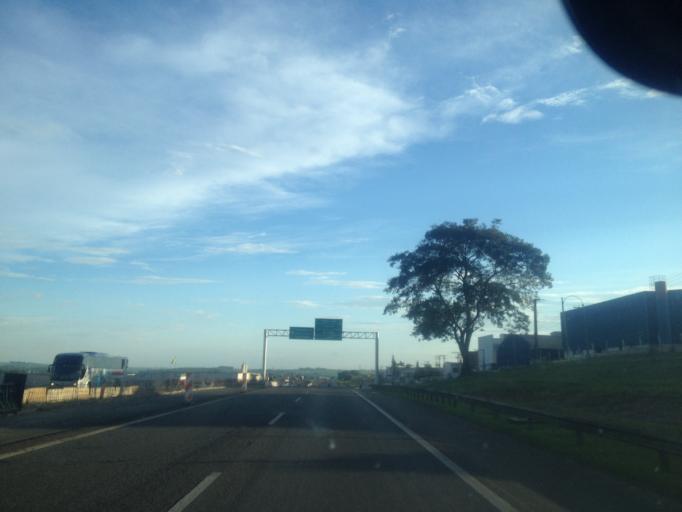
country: BR
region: Sao Paulo
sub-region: Limeira
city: Limeira
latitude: -22.5763
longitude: -47.3667
